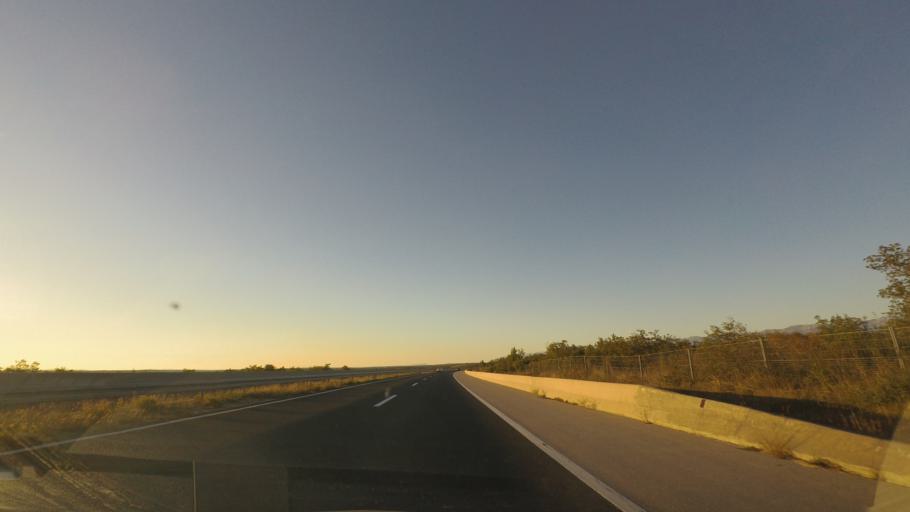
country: HR
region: Zadarska
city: Galovac
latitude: 44.1262
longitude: 15.4275
